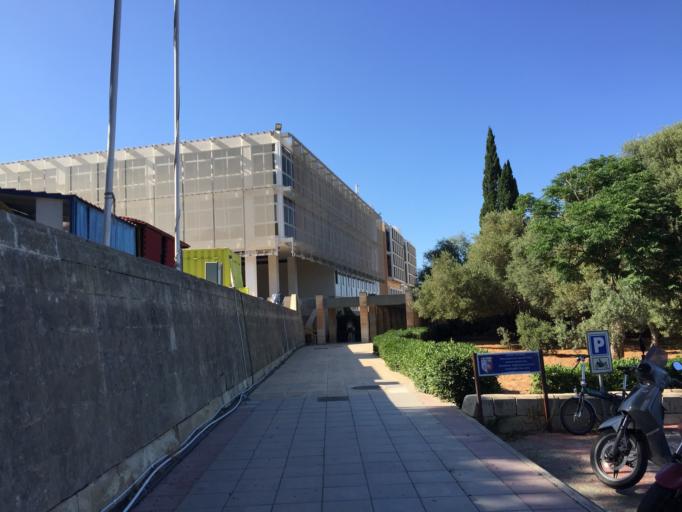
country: MT
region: Il-Gzira
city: Gzira
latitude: 35.9020
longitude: 14.4836
